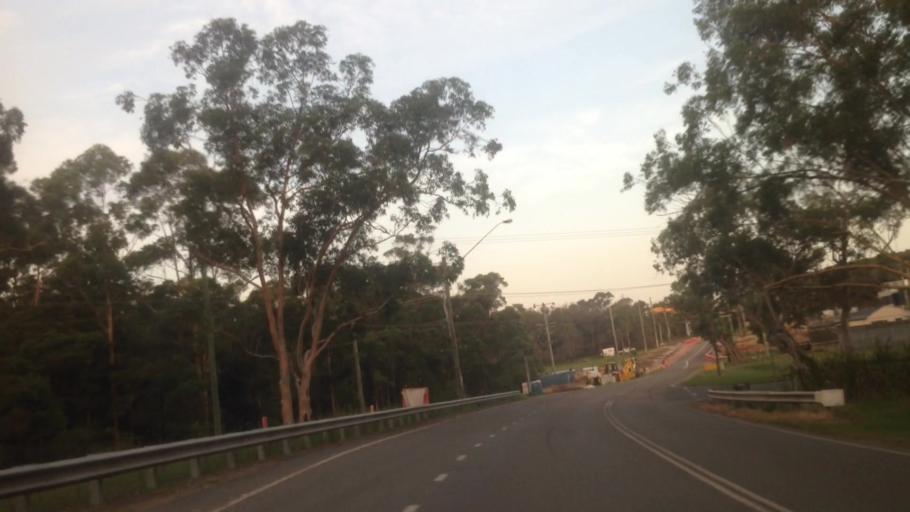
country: AU
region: New South Wales
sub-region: Lake Macquarie Shire
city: Cooranbong
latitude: -33.0712
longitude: 151.4739
